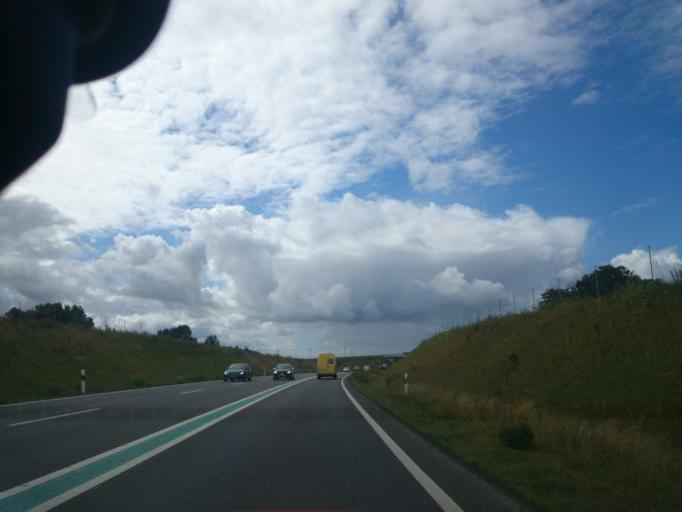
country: DE
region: Mecklenburg-Vorpommern
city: Samtens
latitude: 54.3527
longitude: 13.3024
